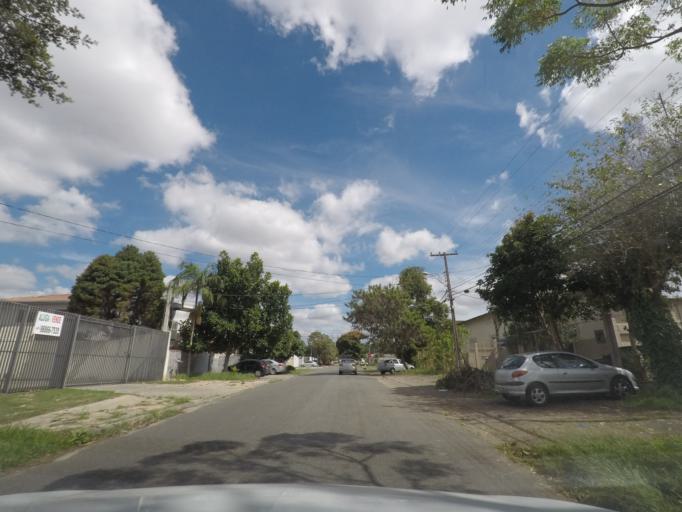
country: BR
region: Parana
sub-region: Sao Jose Dos Pinhais
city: Sao Jose dos Pinhais
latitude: -25.5065
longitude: -49.2289
